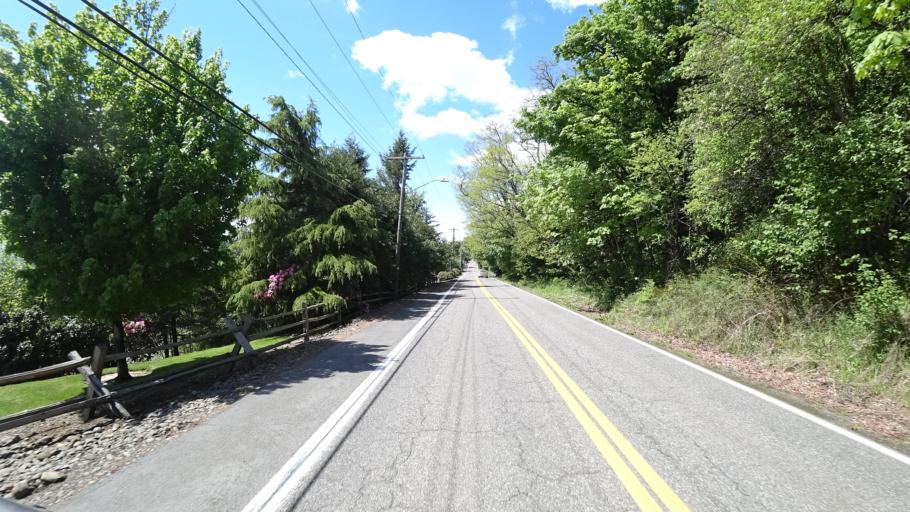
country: US
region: Oregon
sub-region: Washington County
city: West Haven
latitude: 45.5473
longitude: -122.7671
